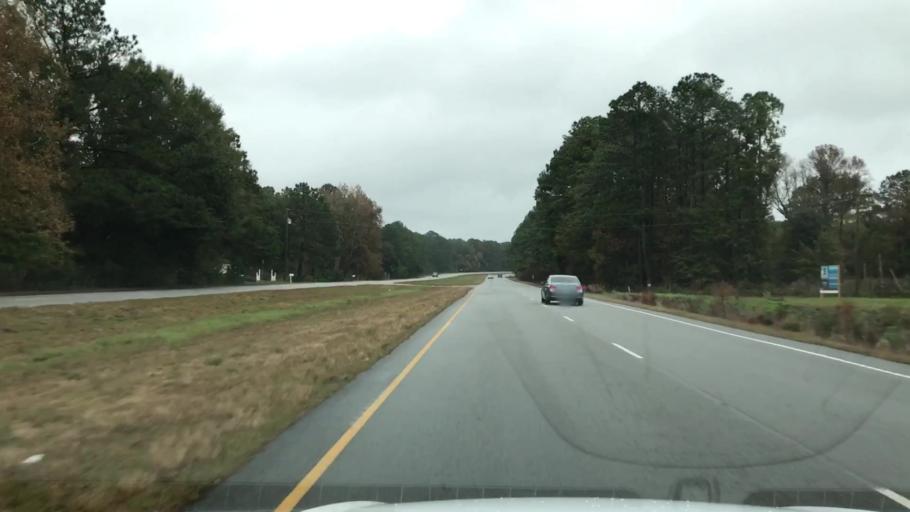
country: US
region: South Carolina
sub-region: Charleston County
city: Awendaw
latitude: 32.9319
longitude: -79.7130
